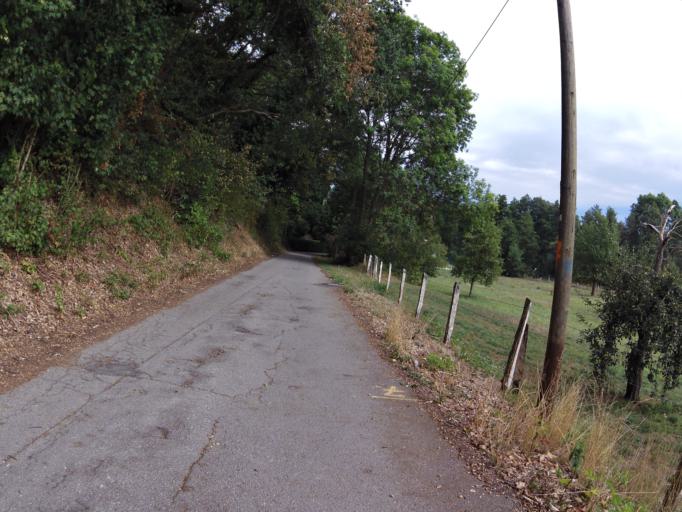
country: DE
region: North Rhine-Westphalia
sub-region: Regierungsbezirk Koln
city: Nideggen
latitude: 50.6752
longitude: 6.4757
